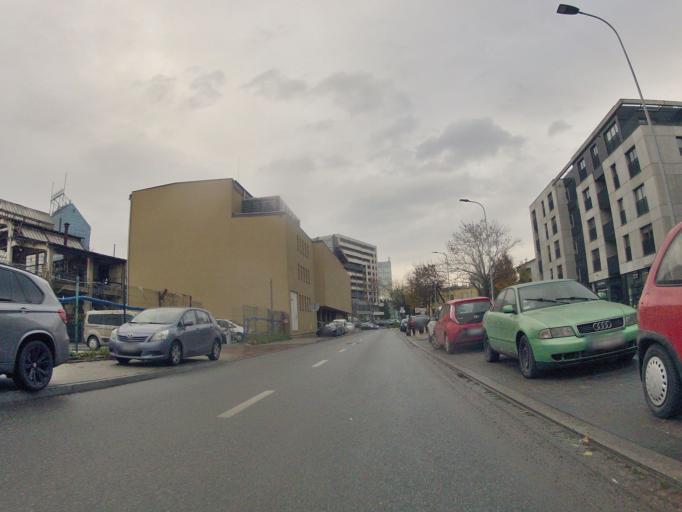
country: PL
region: Lesser Poland Voivodeship
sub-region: Krakow
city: Krakow
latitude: 50.0563
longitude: 19.9646
